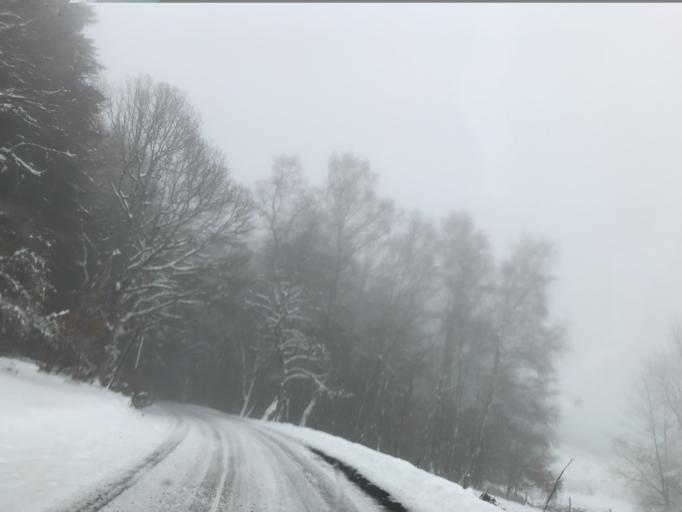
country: FR
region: Rhone-Alpes
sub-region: Departement de la Loire
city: Noiretable
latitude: 45.7358
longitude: 3.6949
